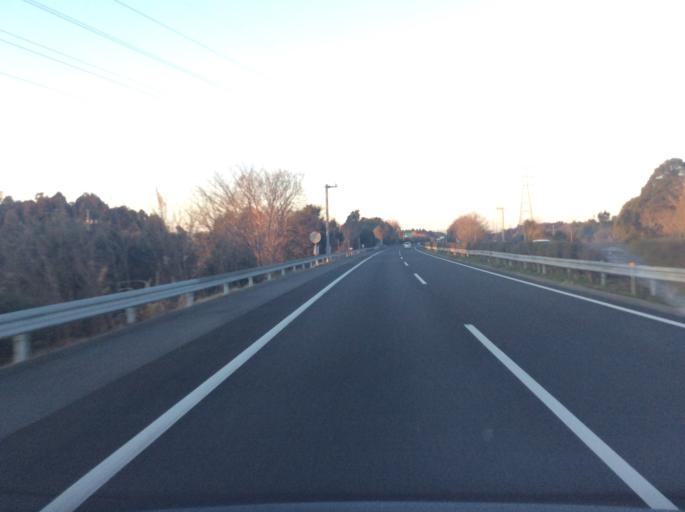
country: JP
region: Ibaraki
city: Hitachi-Naka
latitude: 36.4582
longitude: 140.4835
